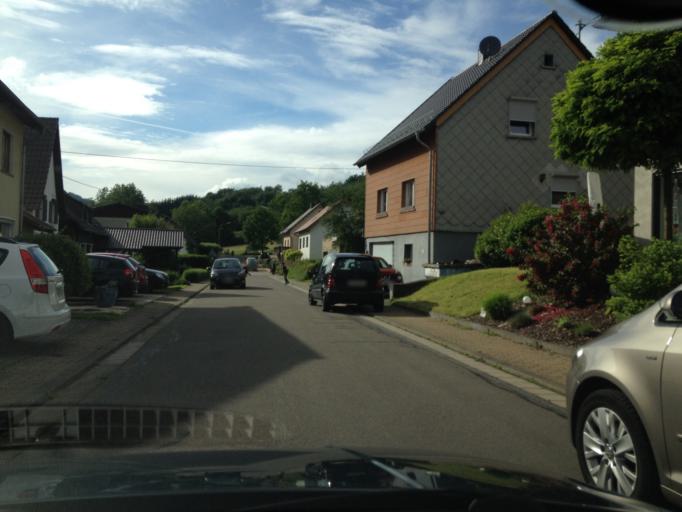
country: DE
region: Saarland
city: Marpingen
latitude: 49.4754
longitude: 7.0646
